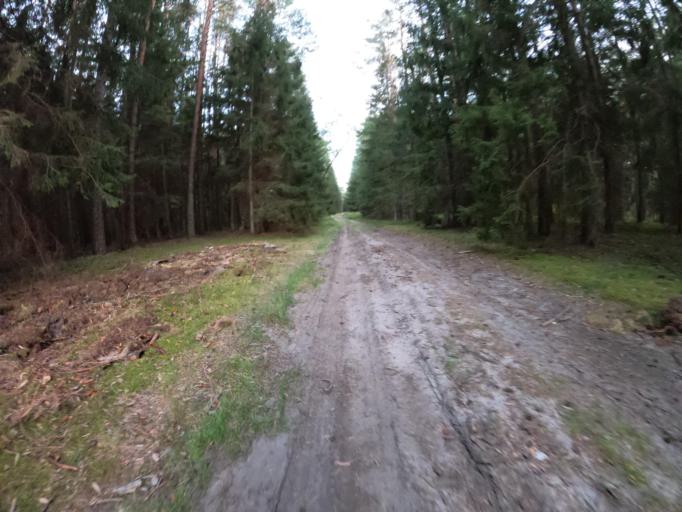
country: PL
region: West Pomeranian Voivodeship
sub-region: Powiat koszalinski
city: Sianow
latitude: 54.0955
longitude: 16.4098
